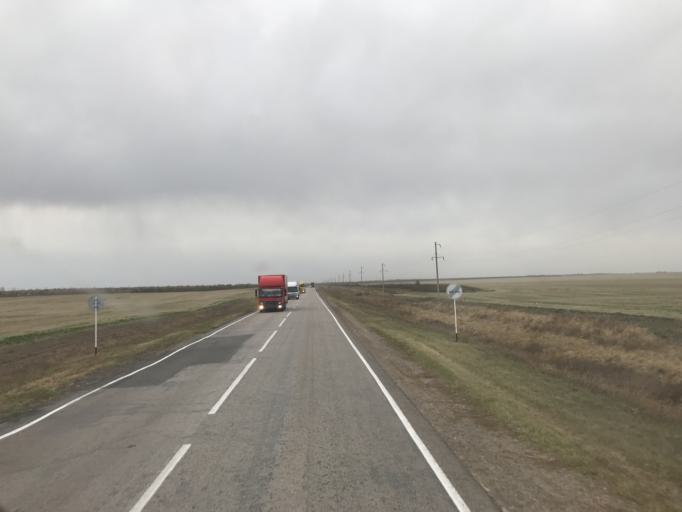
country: KZ
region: Aqmola
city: Zhaqsy
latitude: 51.8083
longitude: 67.7858
